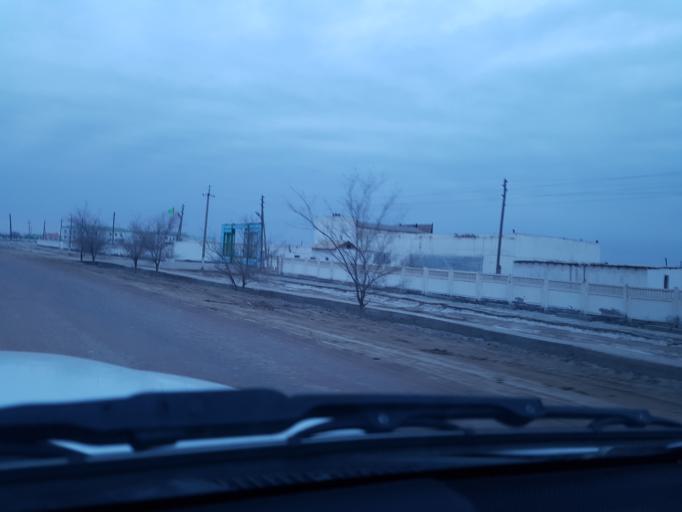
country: TM
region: Dasoguz
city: Yylanly
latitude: 41.8890
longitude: 59.6191
